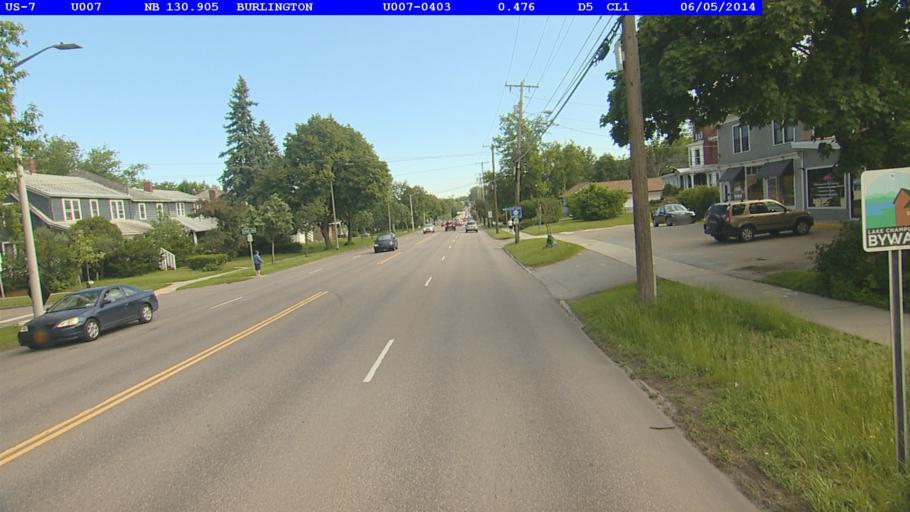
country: US
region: Vermont
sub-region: Chittenden County
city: Burlington
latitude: 44.4526
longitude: -73.2088
